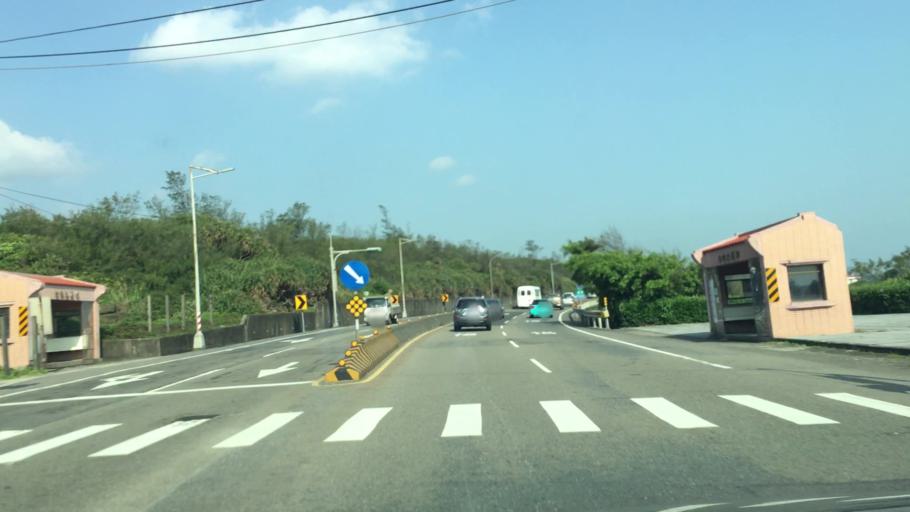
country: TW
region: Taiwan
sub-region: Keelung
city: Keelung
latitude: 25.2071
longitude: 121.6600
